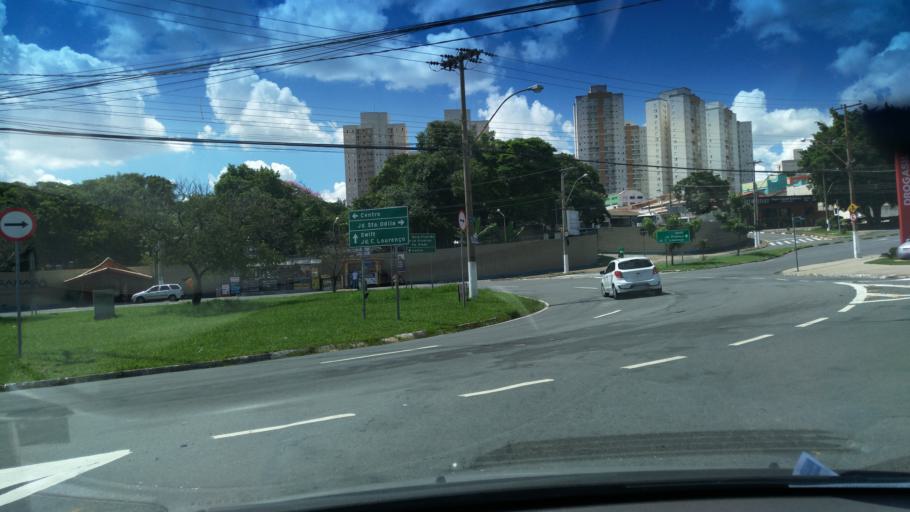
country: BR
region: Sao Paulo
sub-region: Campinas
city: Campinas
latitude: -22.9311
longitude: -47.0377
